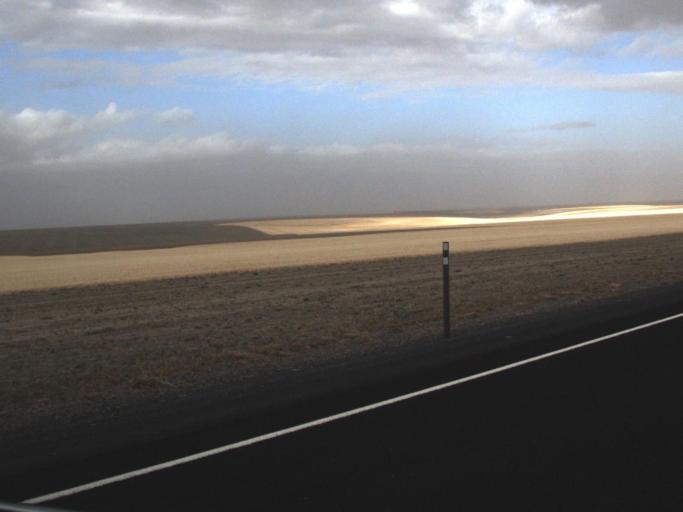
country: US
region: Washington
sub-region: Adams County
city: Ritzville
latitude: 47.3867
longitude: -118.4187
